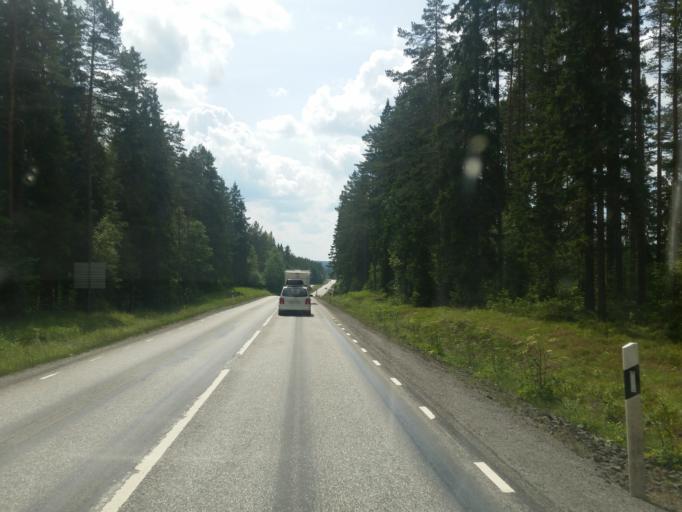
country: SE
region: OErebro
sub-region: Ljusnarsbergs Kommun
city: Kopparberg
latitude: 59.9060
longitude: 15.0211
